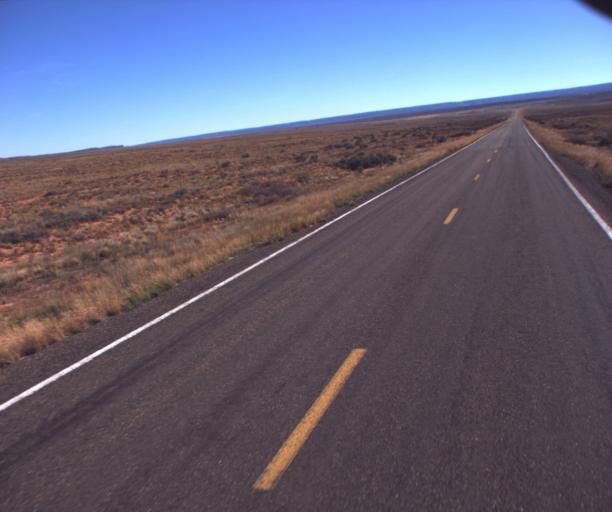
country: US
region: Arizona
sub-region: Coconino County
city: Fredonia
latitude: 36.9284
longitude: -112.4854
